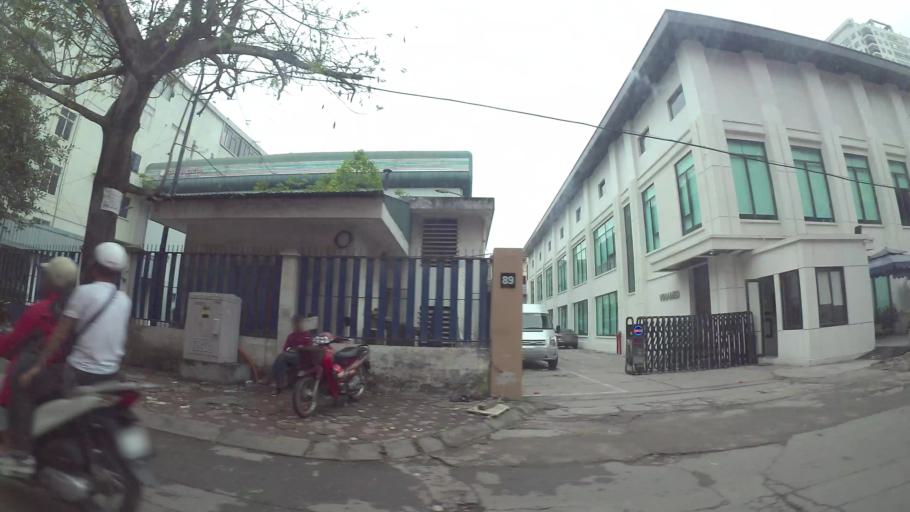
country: VN
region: Ha Noi
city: Hai BaTrung
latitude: 21.0022
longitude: 105.8360
